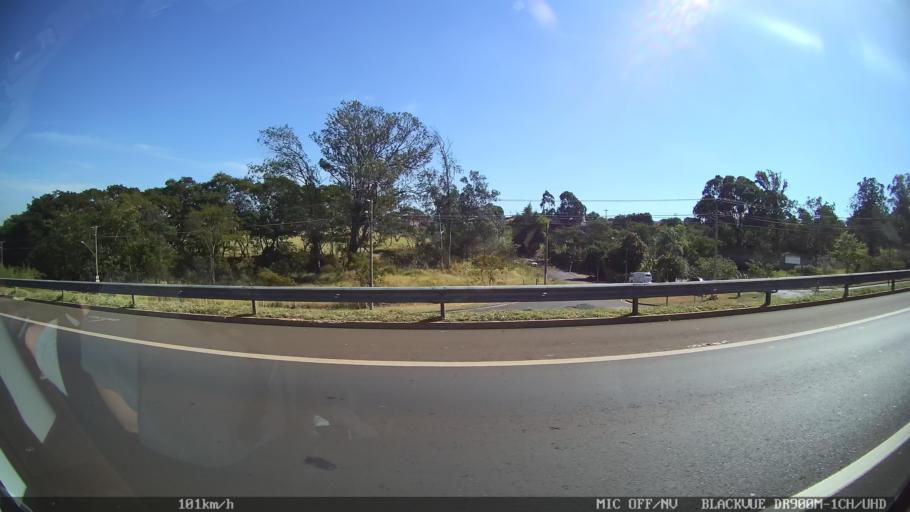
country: BR
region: Sao Paulo
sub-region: Franca
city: Franca
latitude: -20.5091
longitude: -47.4120
